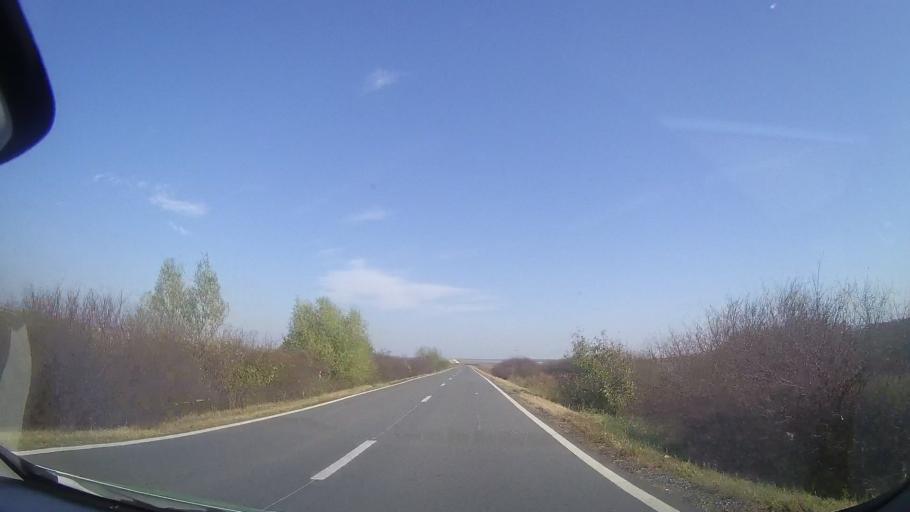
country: RO
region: Timis
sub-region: Comuna Belint
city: Belint
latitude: 45.7714
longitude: 21.7299
